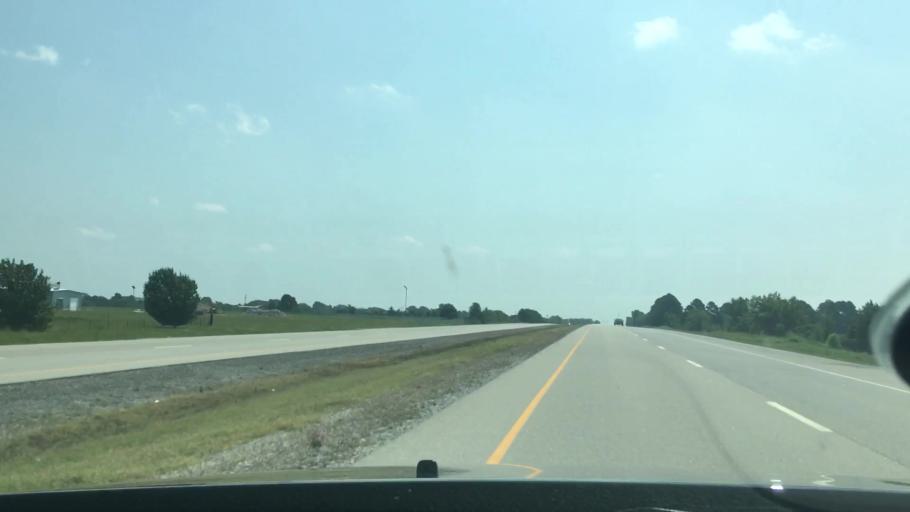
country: US
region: Oklahoma
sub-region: Atoka County
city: Atoka
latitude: 34.3431
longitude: -96.0716
